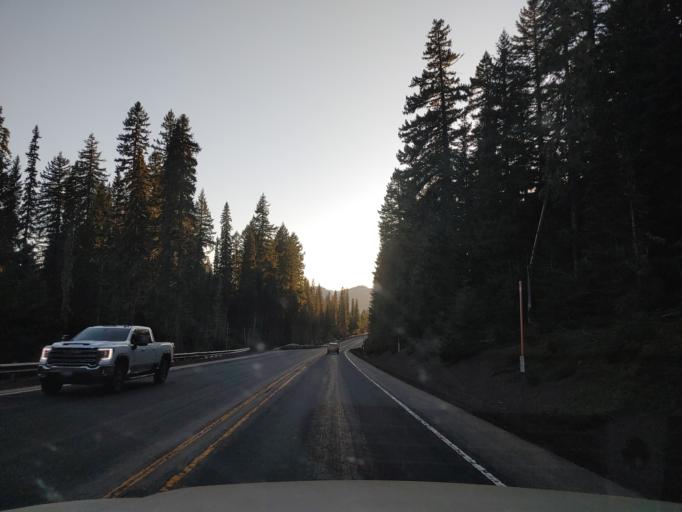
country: US
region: Oregon
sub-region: Lane County
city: Oakridge
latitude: 43.6185
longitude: -122.0787
